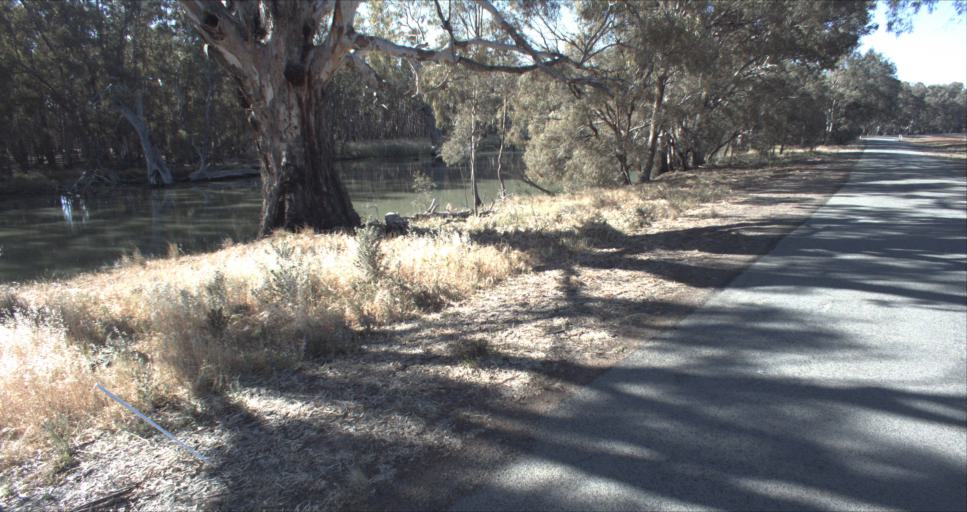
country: AU
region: New South Wales
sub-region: Leeton
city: Leeton
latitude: -34.6106
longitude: 146.2600
